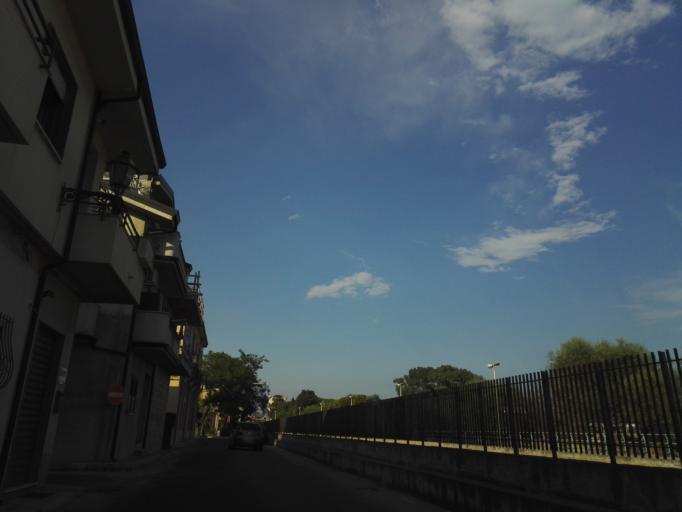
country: IT
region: Calabria
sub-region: Provincia di Reggio Calabria
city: Siderno
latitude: 38.2700
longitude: 16.3011
